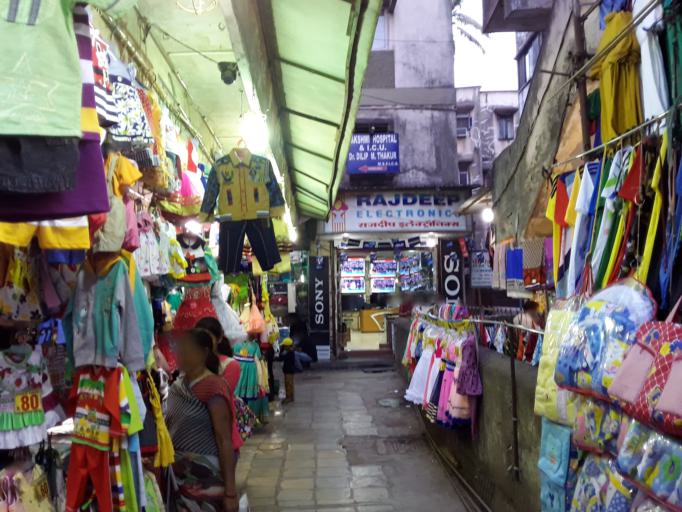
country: IN
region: Maharashtra
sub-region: Thane
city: Dombivli
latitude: 19.2178
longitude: 73.0870
